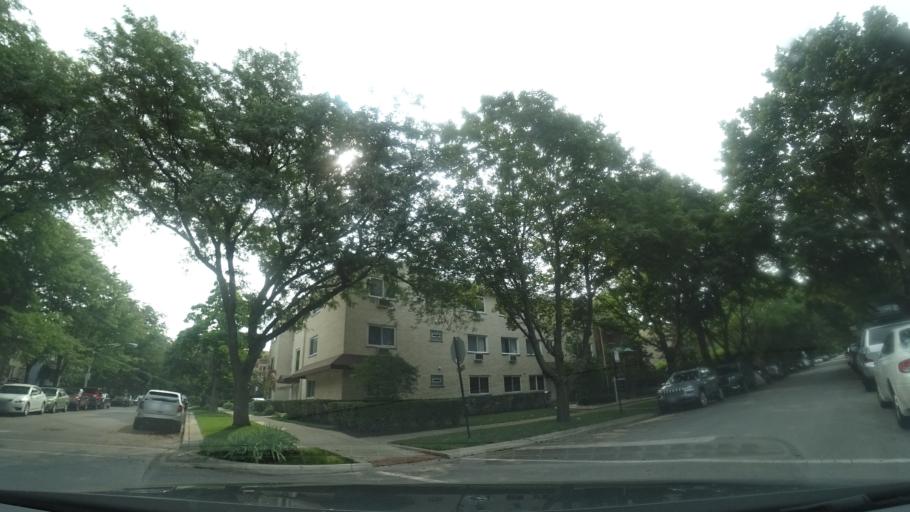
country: US
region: Illinois
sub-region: Cook County
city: Lincolnwood
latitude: 41.9807
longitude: -87.6723
